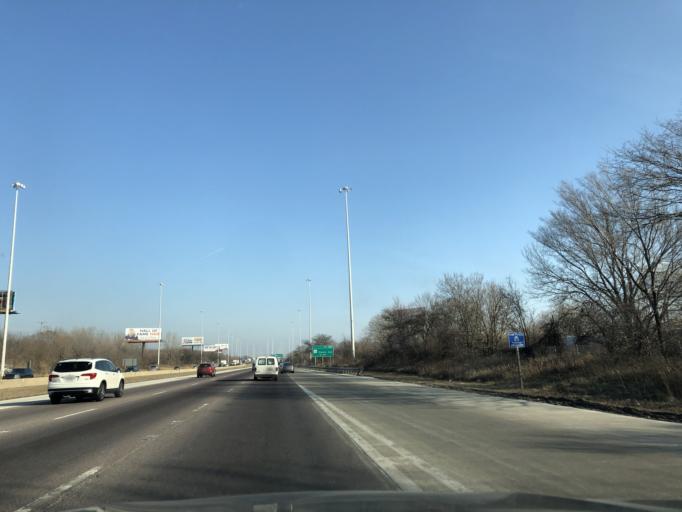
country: US
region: Illinois
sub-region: Cook County
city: Stickney
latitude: 41.8130
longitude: -87.7557
